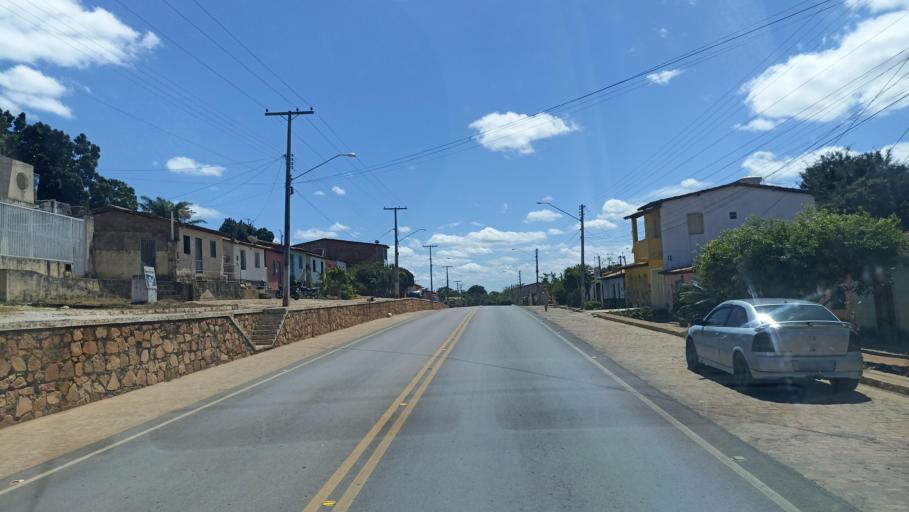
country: BR
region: Bahia
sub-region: Andarai
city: Vera Cruz
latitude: -12.7947
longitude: -41.3280
